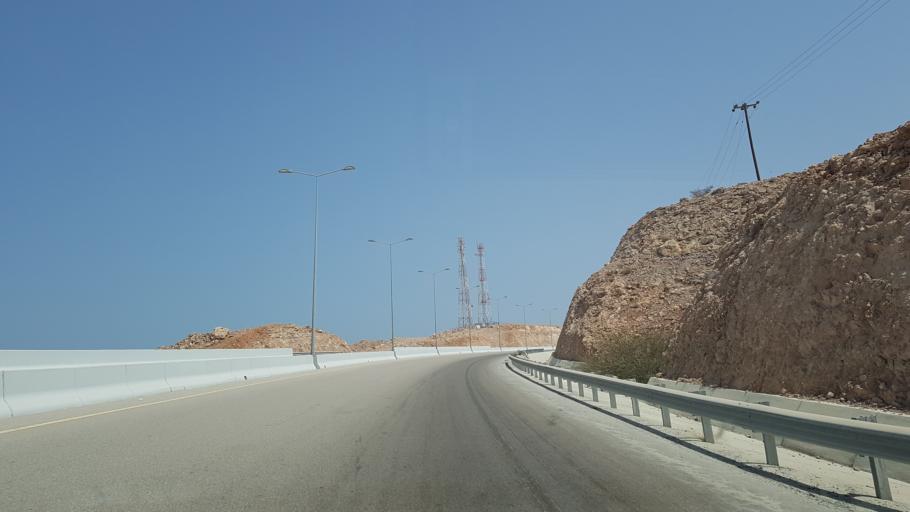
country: OM
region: Muhafazat Masqat
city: Muscat
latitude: 23.1776
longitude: 58.9760
